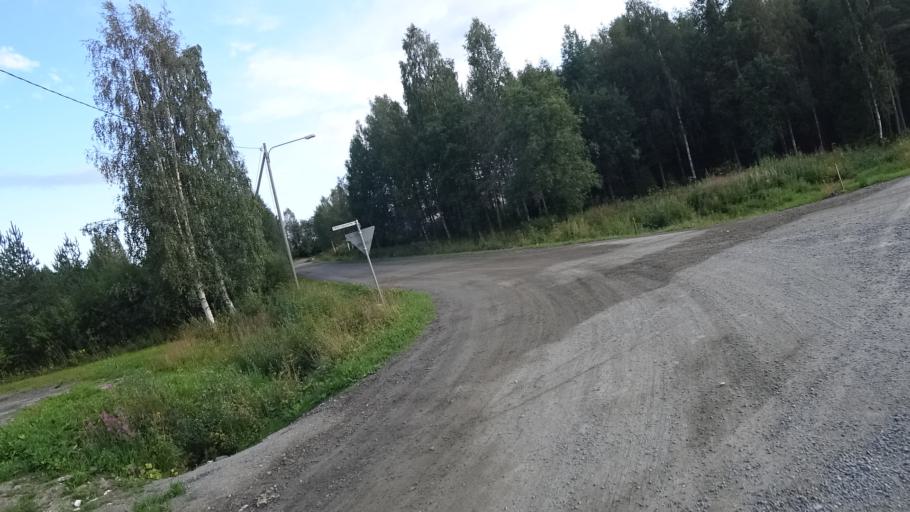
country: FI
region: North Karelia
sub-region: Joensuu
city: Ilomantsi
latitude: 62.6709
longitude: 30.9472
